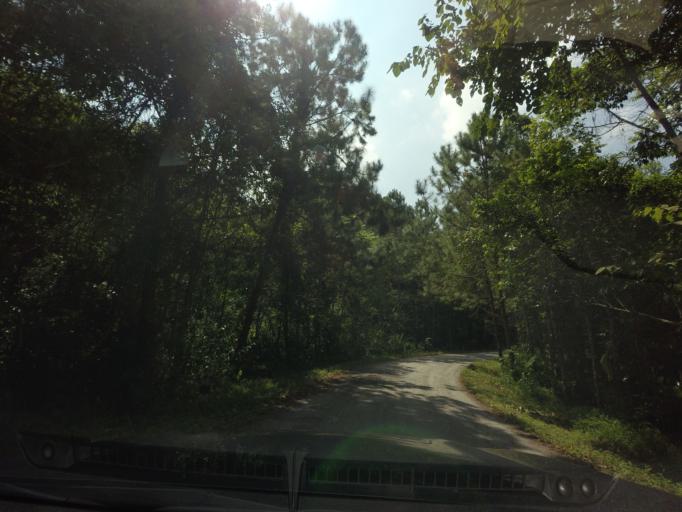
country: TH
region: Loei
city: Na Haeo
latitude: 17.4797
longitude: 100.9393
